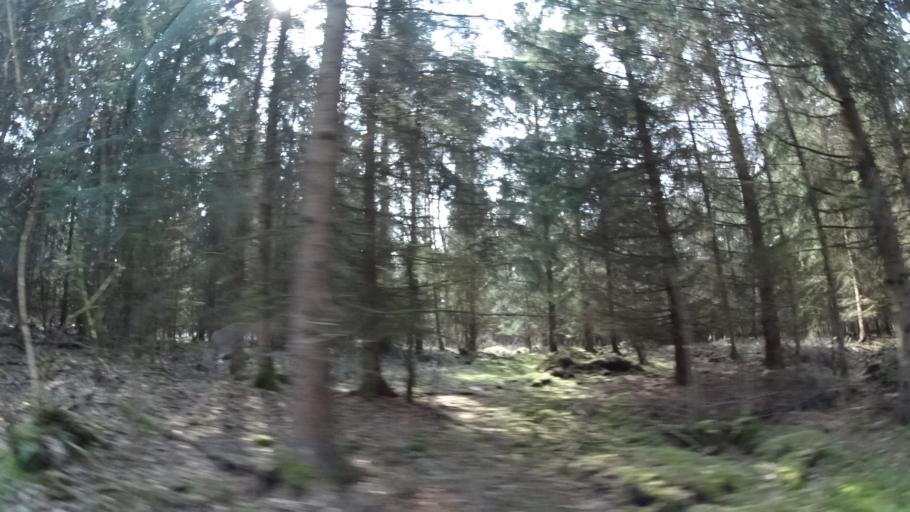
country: DE
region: Rheinland-Pfalz
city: Ruschberg
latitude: 49.6074
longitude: 7.2781
